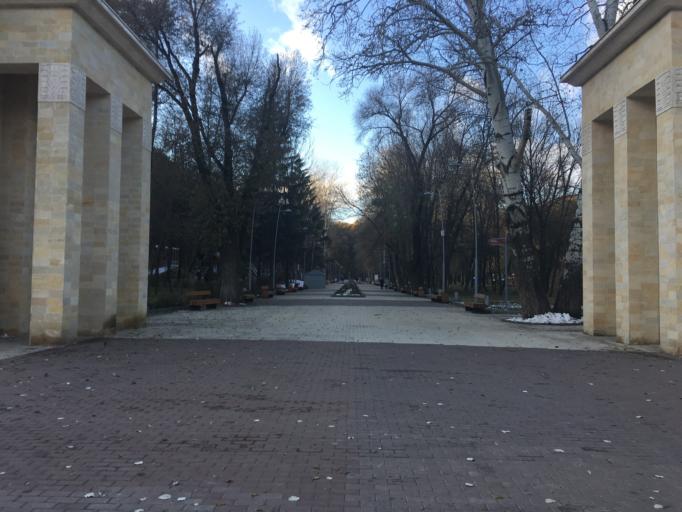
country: RU
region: Voronezj
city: Voronezh
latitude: 51.6964
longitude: 39.2229
